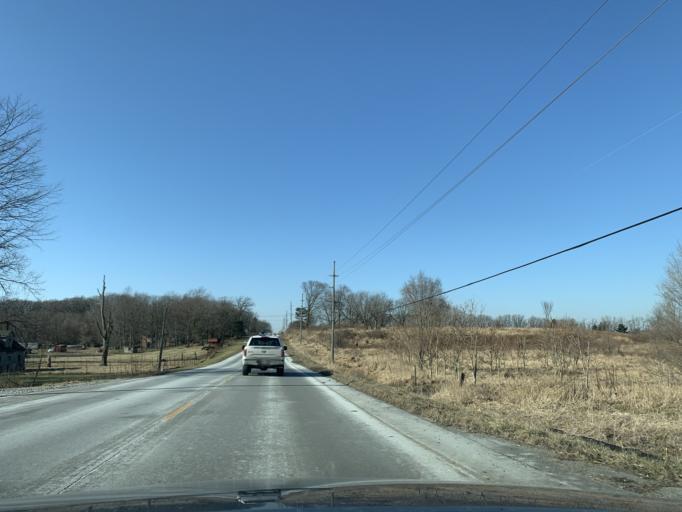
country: US
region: Indiana
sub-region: Lake County
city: Crown Point
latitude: 41.4207
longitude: -87.4041
